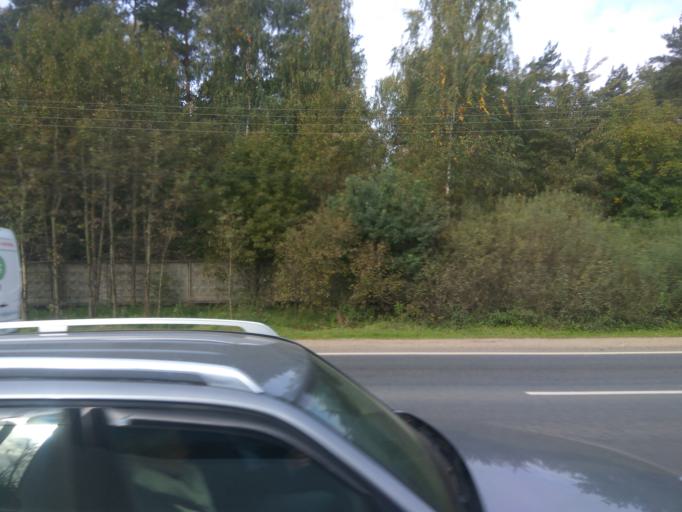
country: RU
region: Moskovskaya
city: Medvezh'i Ozera
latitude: 55.8717
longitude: 37.9949
